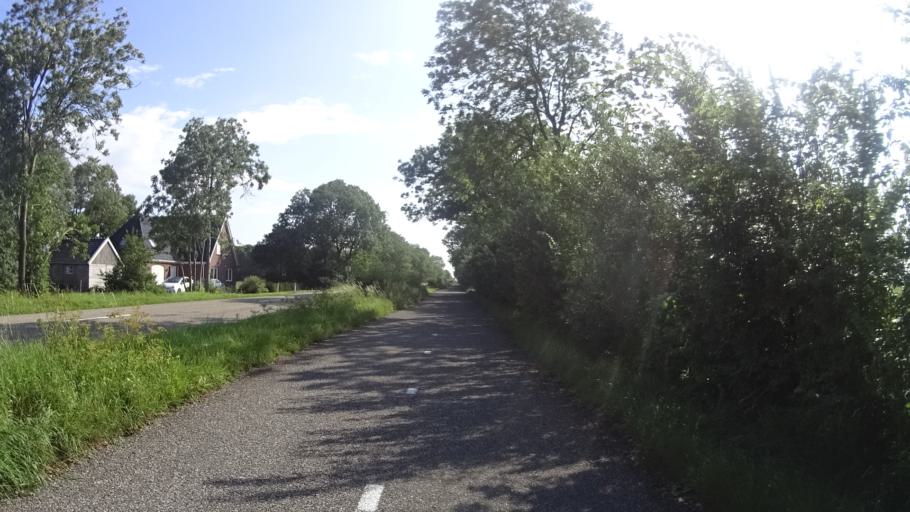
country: NL
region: Friesland
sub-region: Gemeente Franekeradeel
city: Franeker
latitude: 53.1899
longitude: 5.5734
